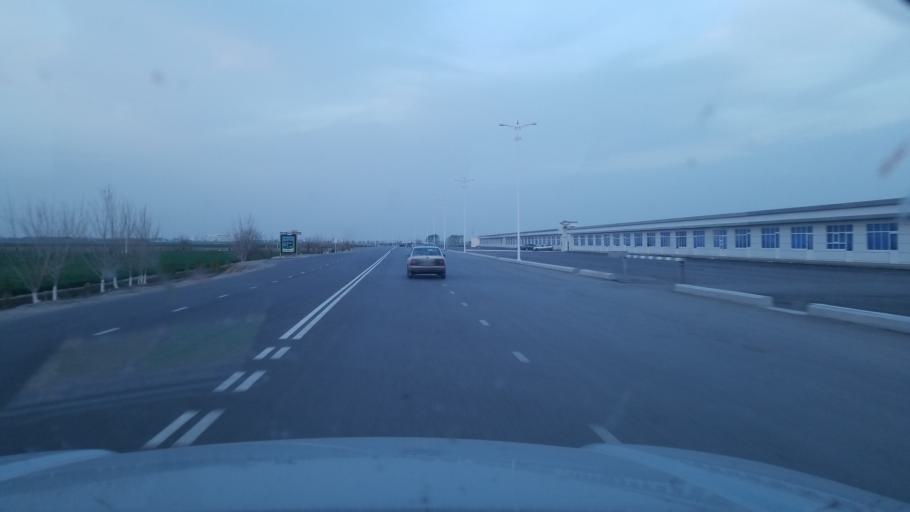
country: TM
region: Lebap
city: Turkmenabat
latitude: 38.9921
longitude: 63.5815
